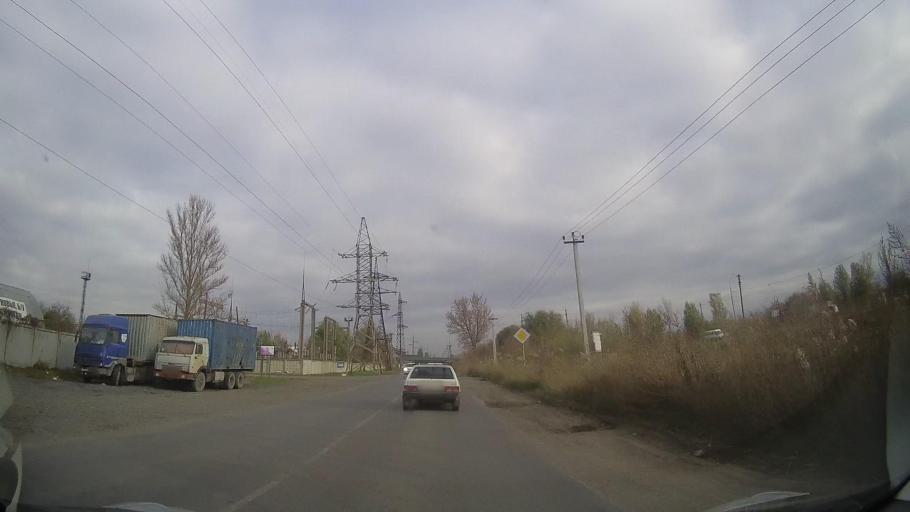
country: RU
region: Rostov
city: Bataysk
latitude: 47.1086
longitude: 39.7642
